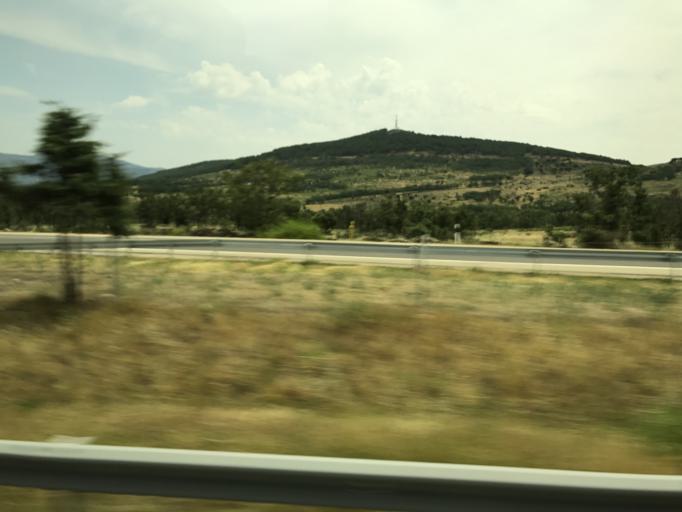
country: ES
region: Madrid
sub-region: Provincia de Madrid
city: Buitrago del Lozoya
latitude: 40.9673
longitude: -3.6410
